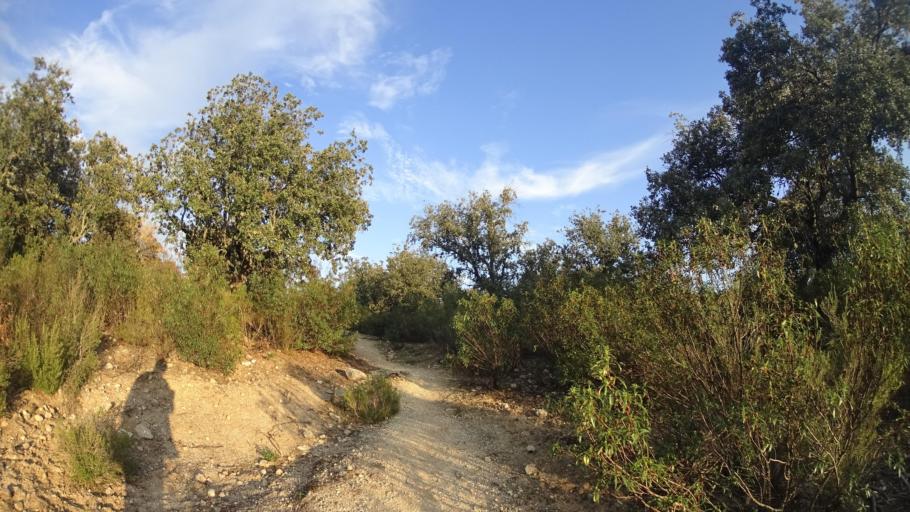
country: ES
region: Madrid
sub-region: Provincia de Madrid
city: Colmenarejo
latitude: 40.5605
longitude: -4.0423
